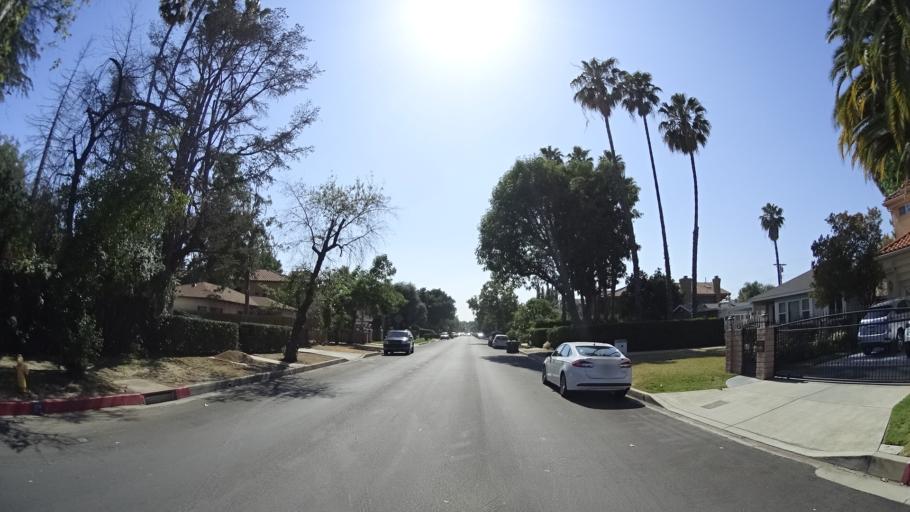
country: US
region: California
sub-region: Los Angeles County
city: Sherman Oaks
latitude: 34.1612
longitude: -118.4532
